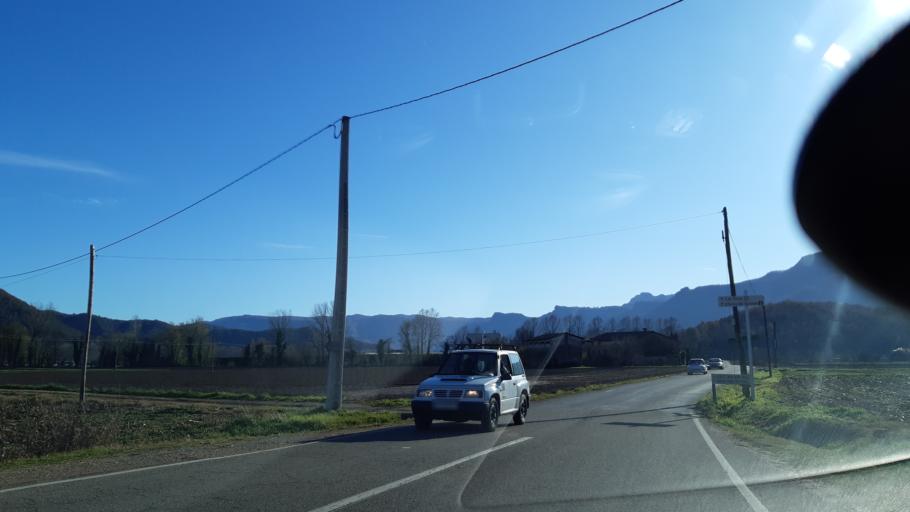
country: ES
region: Catalonia
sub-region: Provincia de Girona
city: Bas
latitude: 42.1465
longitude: 2.4413
